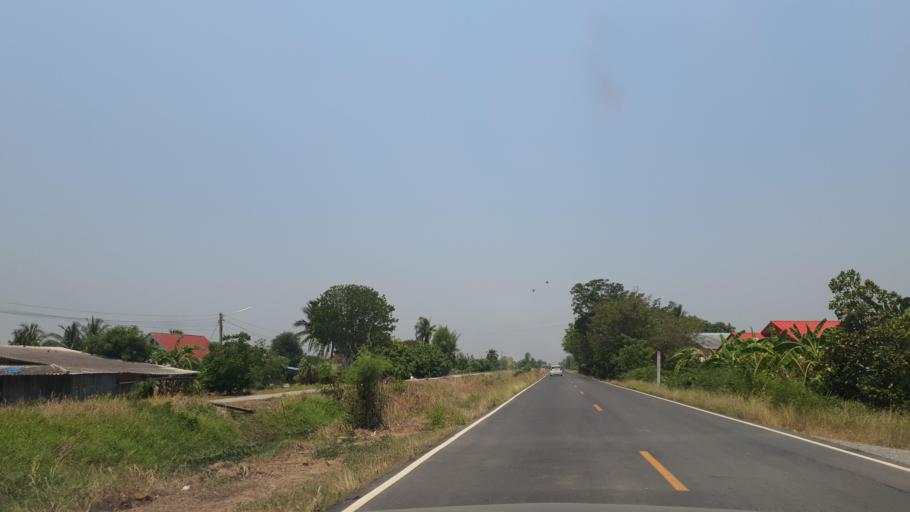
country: TH
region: Suphan Buri
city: Si Prachan
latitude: 14.6229
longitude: 100.0956
